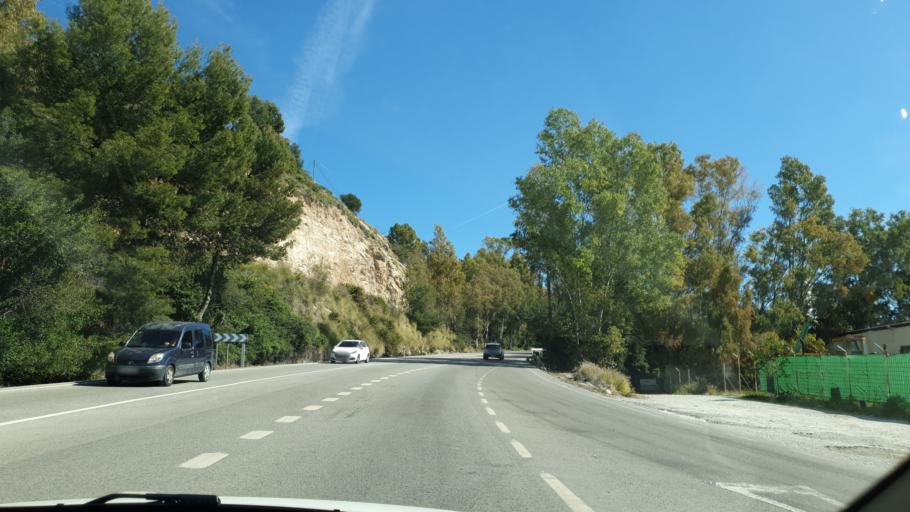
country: ES
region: Andalusia
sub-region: Provincia de Malaga
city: Marbella
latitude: 36.5326
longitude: -4.8733
